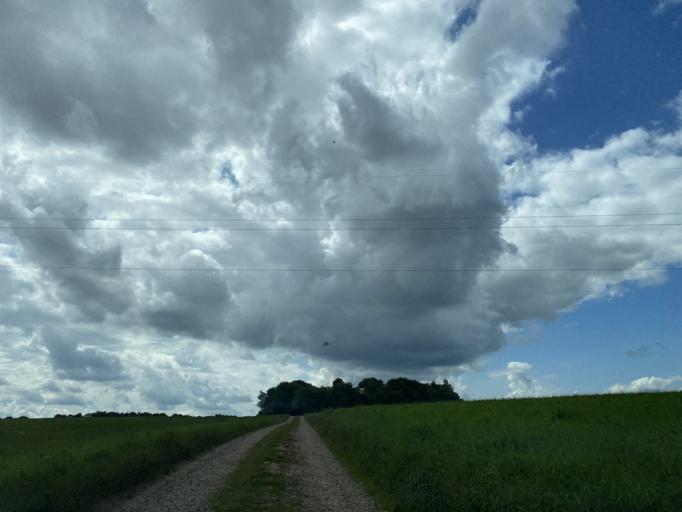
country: DK
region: Central Jutland
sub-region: Silkeborg Kommune
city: Silkeborg
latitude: 56.2129
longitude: 9.5751
